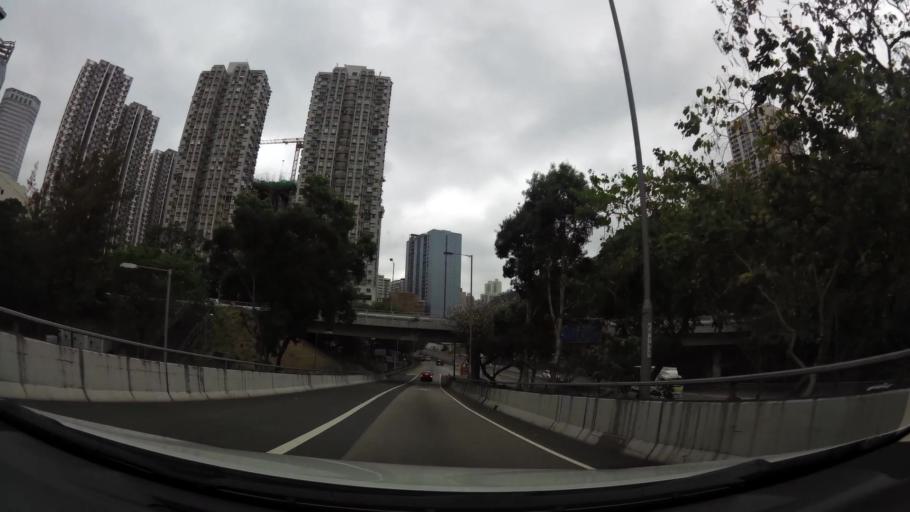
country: HK
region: Tsuen Wan
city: Tsuen Wan
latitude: 22.3544
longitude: 114.1279
